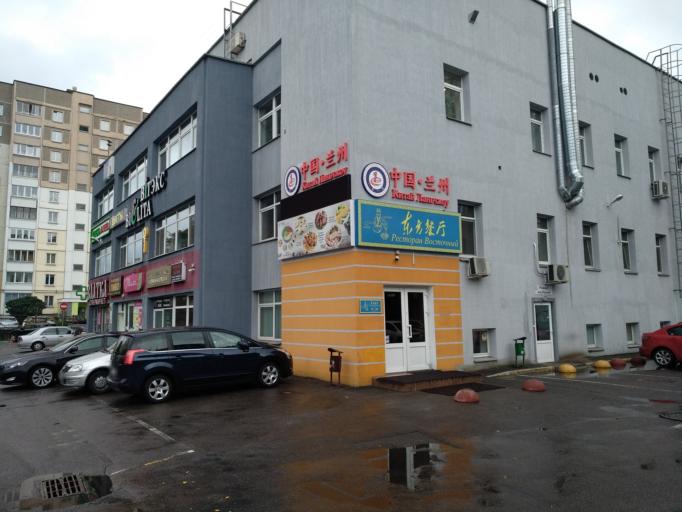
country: BY
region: Minsk
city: Minsk
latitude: 53.9395
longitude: 27.5984
